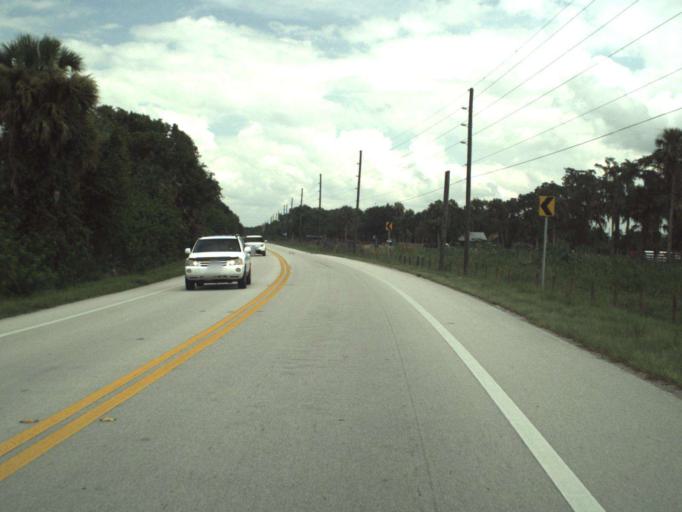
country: US
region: Florida
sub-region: Okeechobee County
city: Taylor Creek
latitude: 27.1001
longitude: -80.6575
